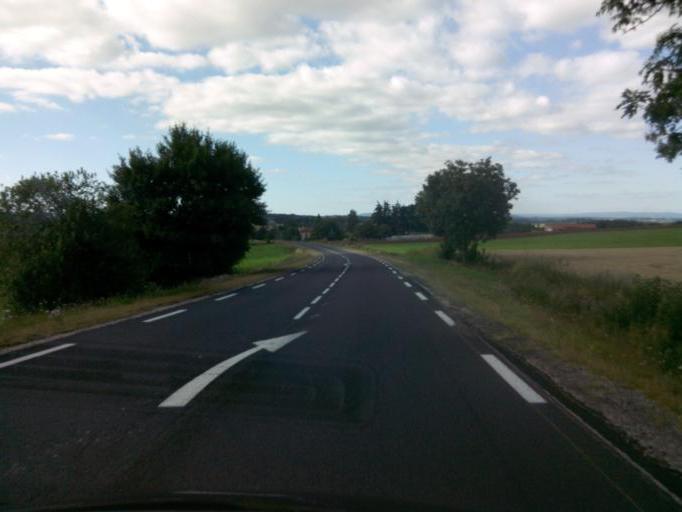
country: FR
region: Auvergne
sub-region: Departement de la Haute-Loire
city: Saint-Paulien
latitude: 45.1845
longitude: 3.8250
